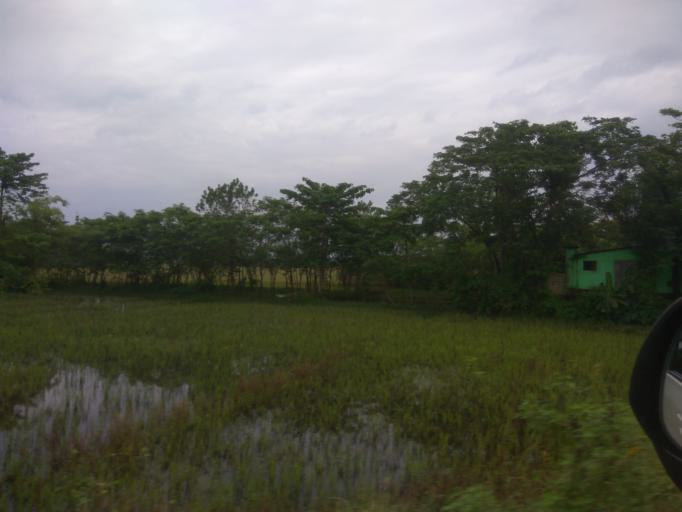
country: IN
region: Assam
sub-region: Karimganj
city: Karimganj
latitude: 24.9499
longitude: 92.2411
